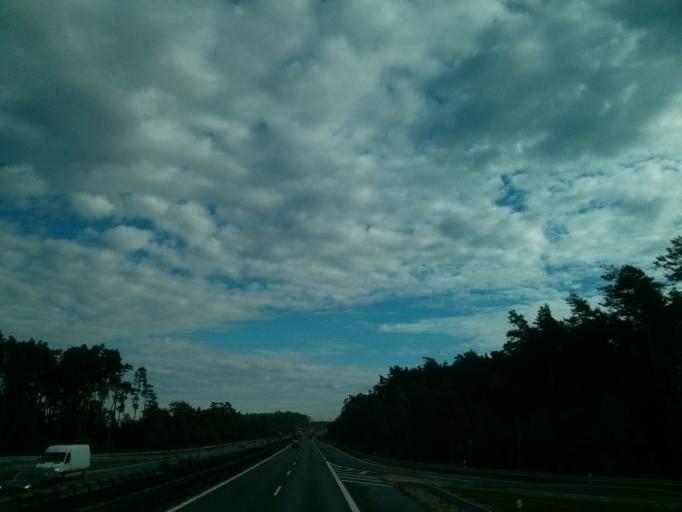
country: DE
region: Bavaria
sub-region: Regierungsbezirk Mittelfranken
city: Heilsbronn
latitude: 49.3098
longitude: 10.8277
